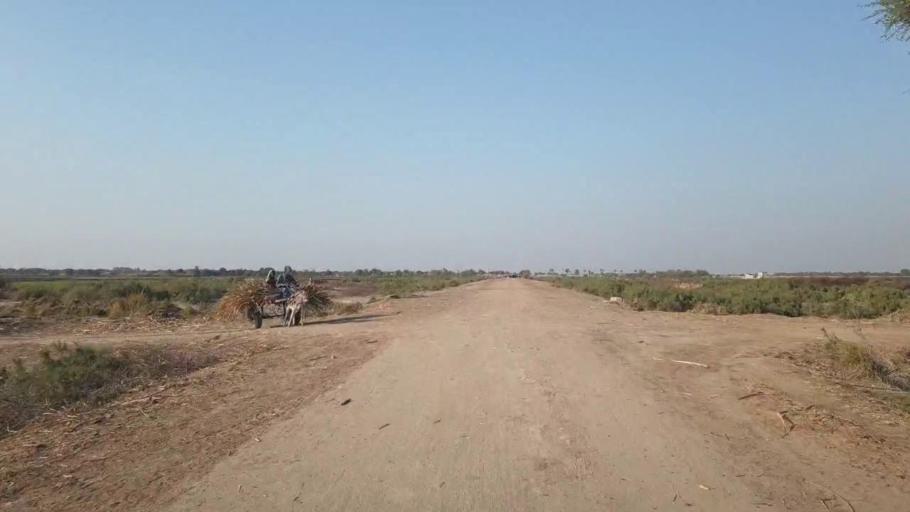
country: PK
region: Sindh
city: Mirpur Khas
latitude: 25.4476
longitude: 68.9340
